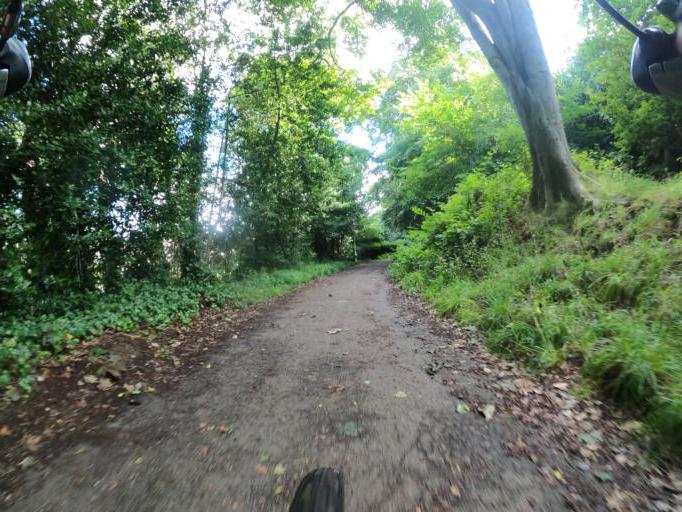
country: GB
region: Scotland
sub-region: Edinburgh
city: Colinton
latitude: 55.9560
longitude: -3.2500
